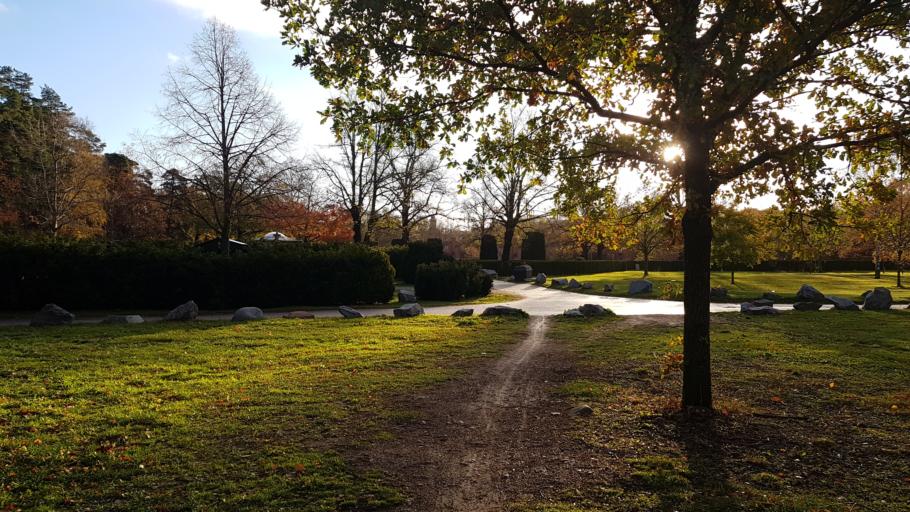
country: SE
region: Stockholm
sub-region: Solna Kommun
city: Solna
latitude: 59.3550
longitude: 18.0167
